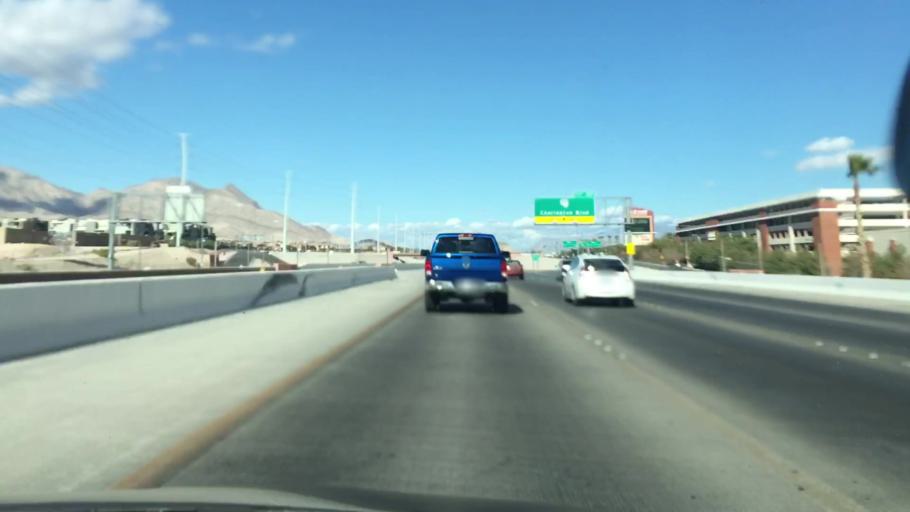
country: US
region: Nevada
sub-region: Clark County
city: Summerlin South
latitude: 36.1536
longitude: -115.3369
